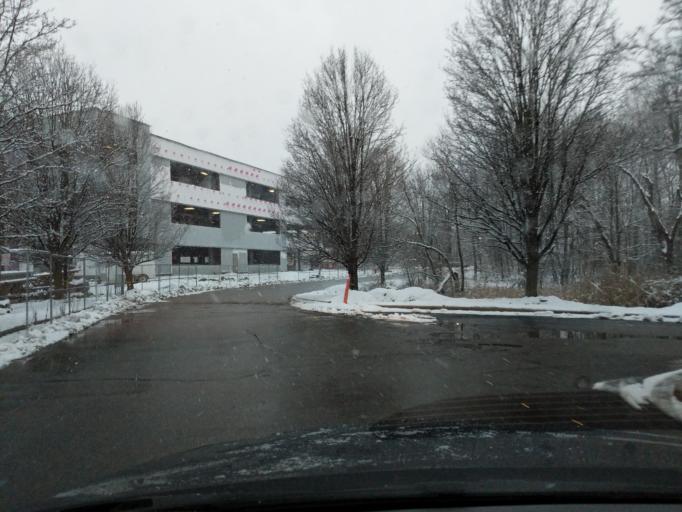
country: US
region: Ohio
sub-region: Summit County
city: Fairlawn
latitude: 41.1023
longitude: -81.5874
